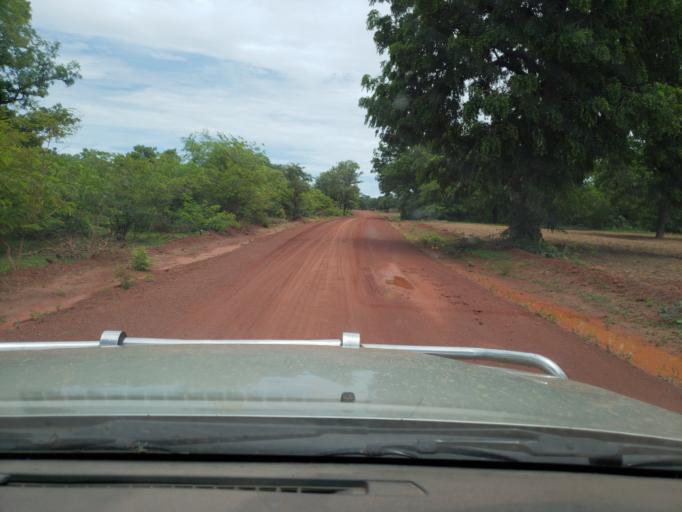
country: ML
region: Sikasso
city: Sikasso
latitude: 11.6804
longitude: -6.3290
